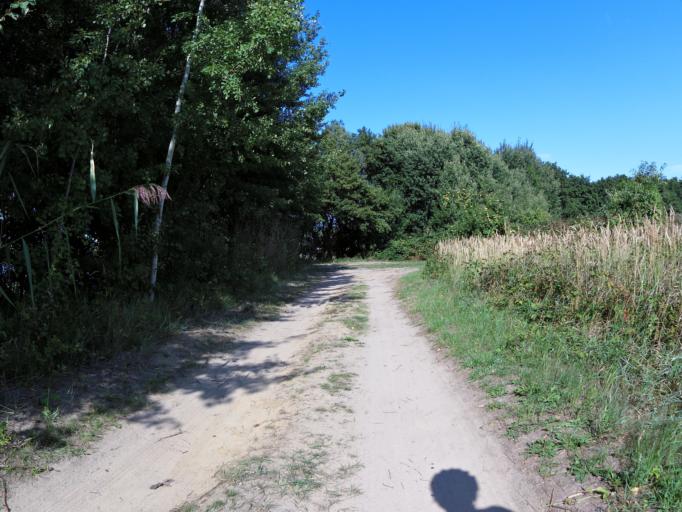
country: DE
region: Mecklenburg-Vorpommern
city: Seebad Bansin
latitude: 53.9648
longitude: 14.1474
